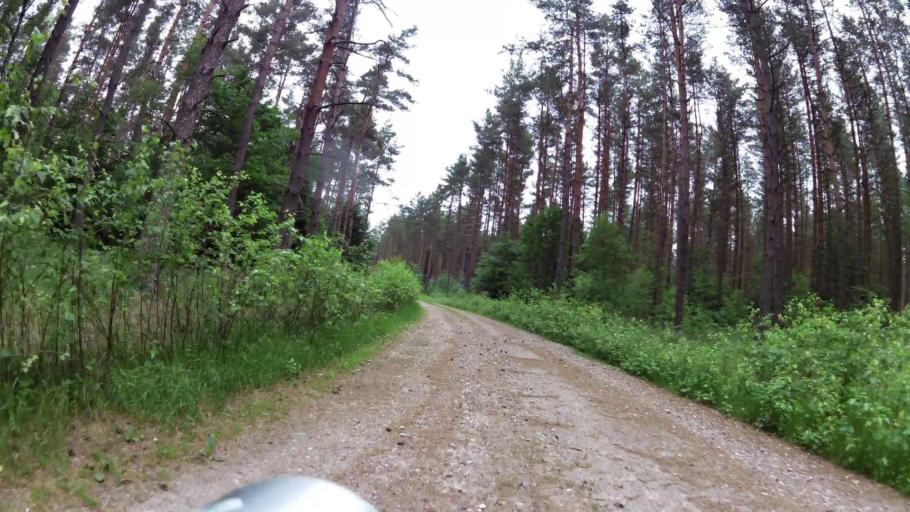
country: PL
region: West Pomeranian Voivodeship
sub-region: Powiat szczecinecki
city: Bialy Bor
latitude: 53.9189
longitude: 16.8312
